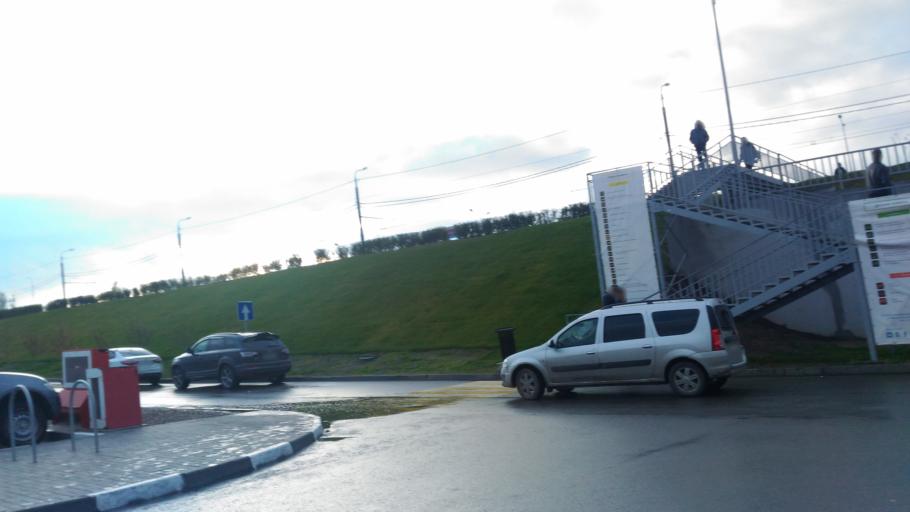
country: RU
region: Volgograd
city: Volgograd
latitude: 48.6378
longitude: 44.4319
